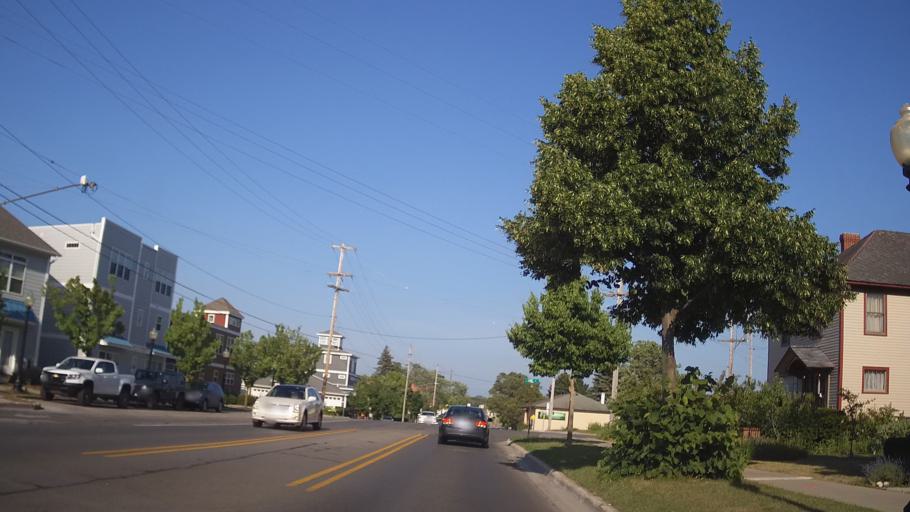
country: US
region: Michigan
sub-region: Grand Traverse County
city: Traverse City
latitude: 44.7594
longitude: -85.6191
